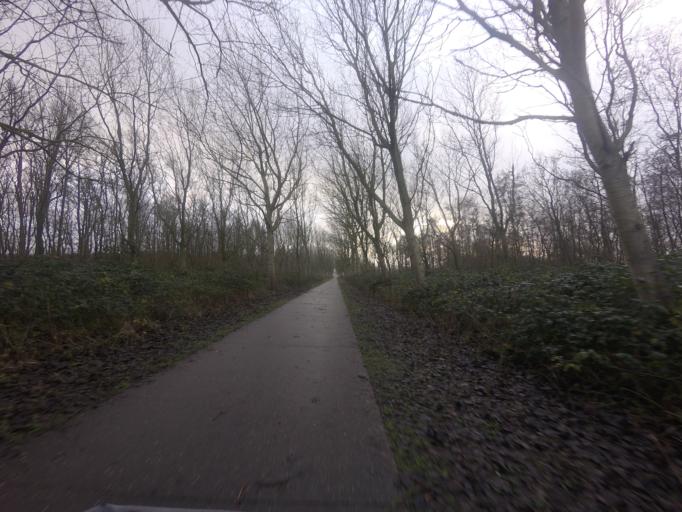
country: NL
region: North Holland
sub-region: Gemeente Texel
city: Den Burg
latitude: 53.1621
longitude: 4.8520
